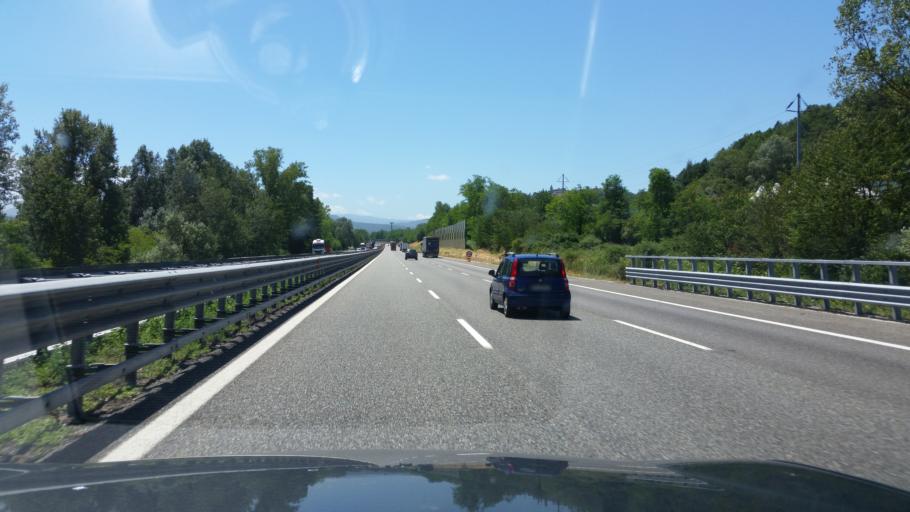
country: IT
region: Piedmont
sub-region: Provincia di Alessandria
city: Silvano d'Orba
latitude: 44.6853
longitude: 8.6625
